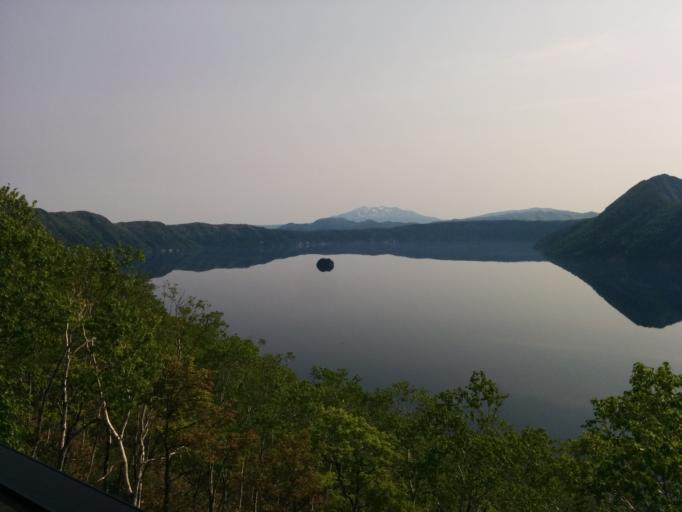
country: JP
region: Hokkaido
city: Bihoro
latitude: 43.5561
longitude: 144.5074
